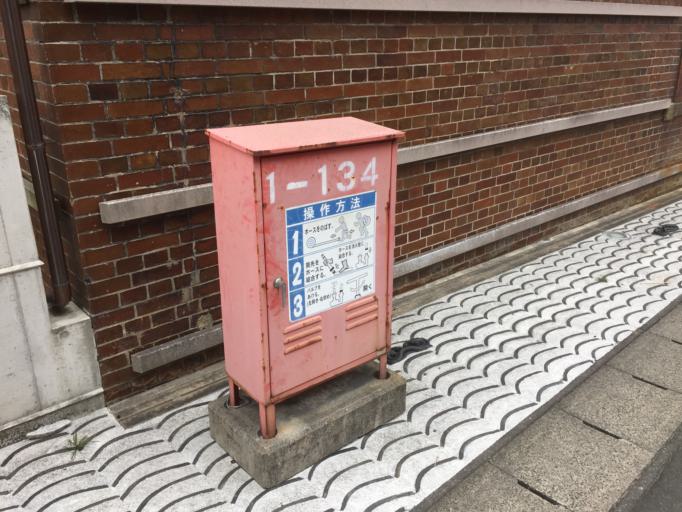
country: JP
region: Shizuoka
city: Kosai-shi
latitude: 34.7181
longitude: 137.5421
